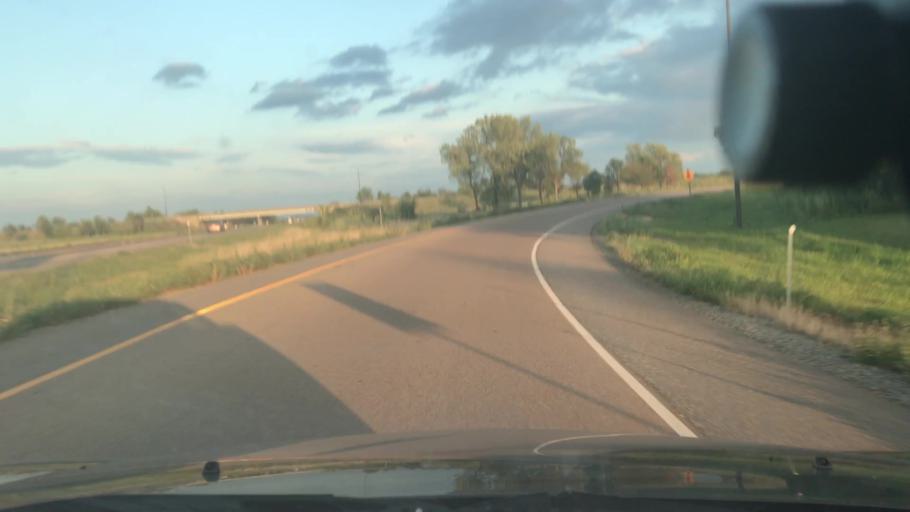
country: US
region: Illinois
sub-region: Washington County
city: Okawville
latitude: 38.4416
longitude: -89.5343
